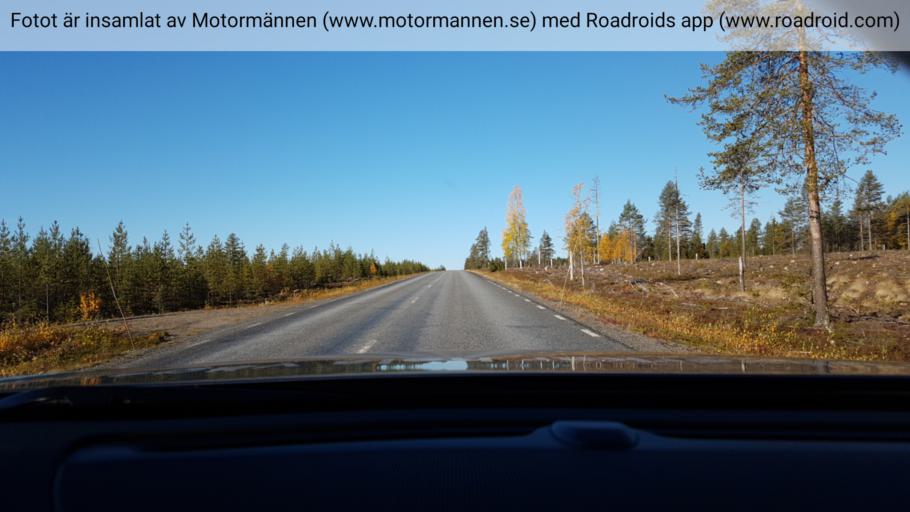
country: SE
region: Vaesterbotten
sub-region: Skelleftea Kommun
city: Boliden
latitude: 65.3824
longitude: 20.1576
